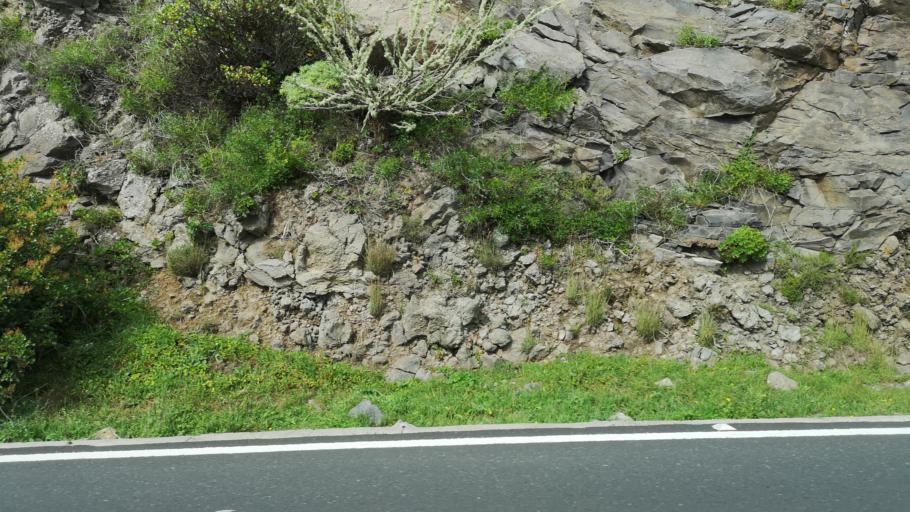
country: ES
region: Canary Islands
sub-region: Provincia de Santa Cruz de Tenerife
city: Alajero
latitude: 28.0998
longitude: -17.1915
